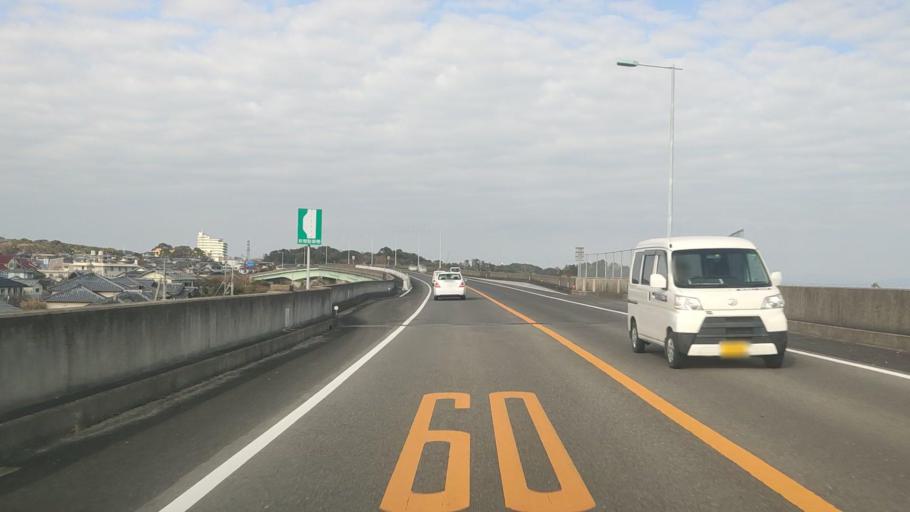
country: JP
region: Nagasaki
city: Shimabara
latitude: 32.7521
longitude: 130.3741
